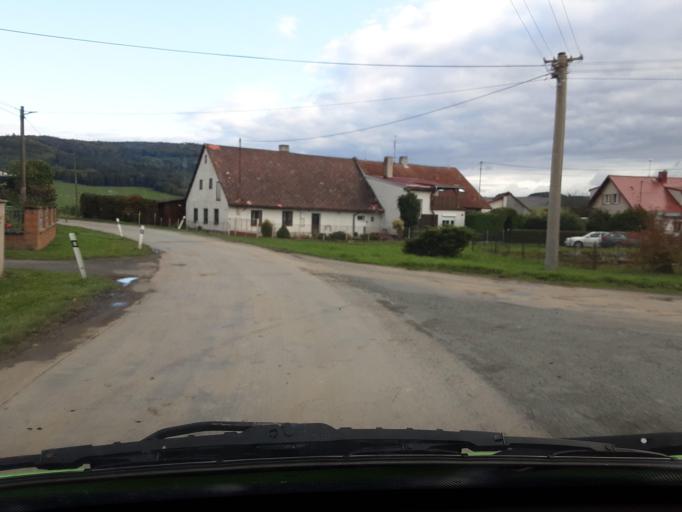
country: CZ
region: Plzensky
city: Janovice nad Uhlavou
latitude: 49.4186
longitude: 13.1609
